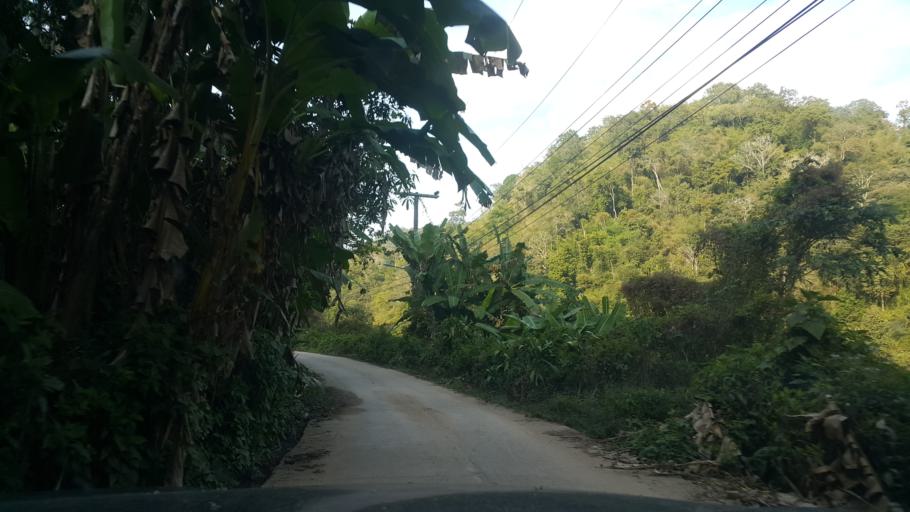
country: TH
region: Chiang Mai
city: Samoeng
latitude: 19.0039
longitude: 98.6720
